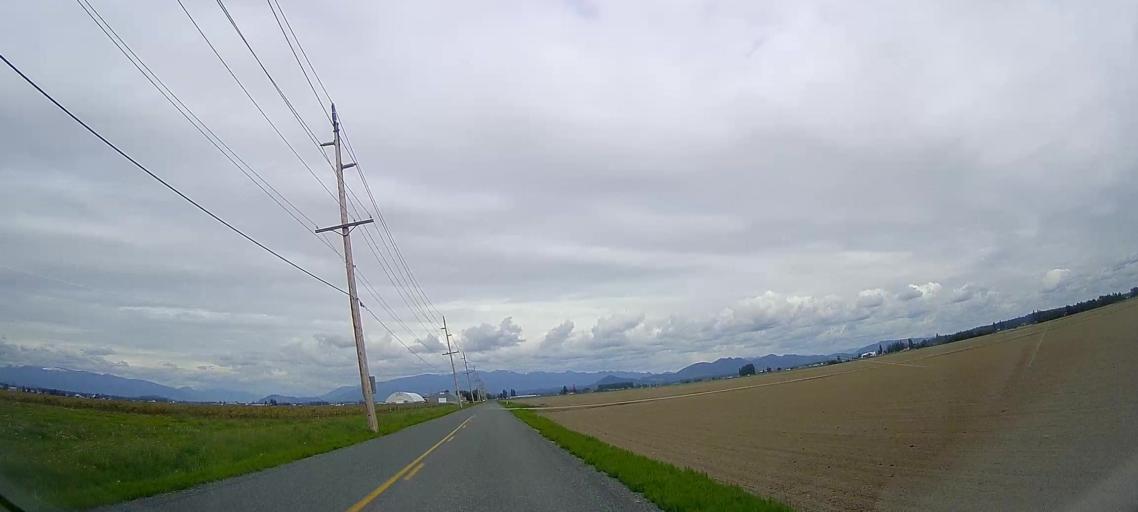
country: US
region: Washington
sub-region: Skagit County
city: Anacortes
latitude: 48.4209
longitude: -122.4970
